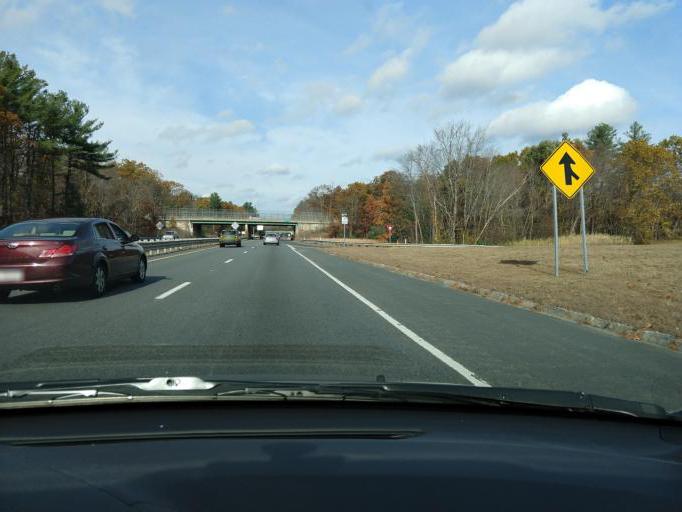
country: US
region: Massachusetts
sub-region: Middlesex County
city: Acton
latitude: 42.4767
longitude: -71.4474
